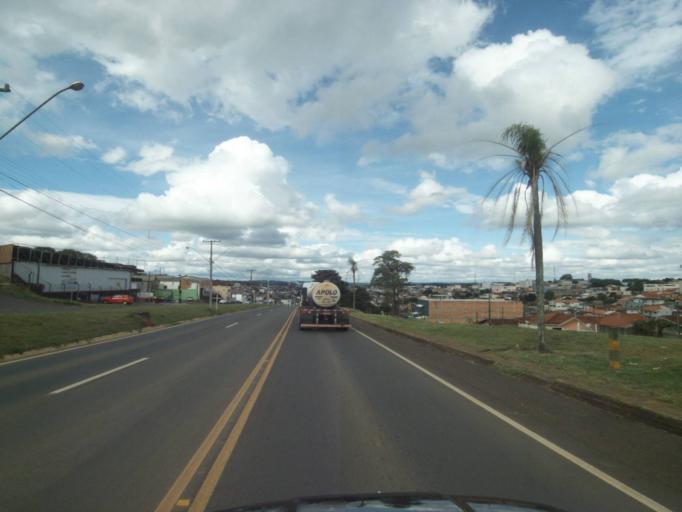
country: BR
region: Parana
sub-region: Telemaco Borba
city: Telemaco Borba
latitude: -24.3301
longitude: -50.6380
